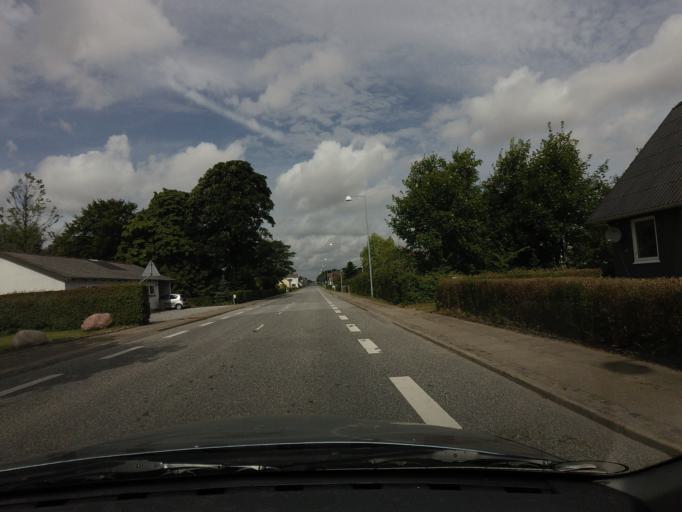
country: DK
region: North Denmark
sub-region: Hjorring Kommune
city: Sindal
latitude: 57.3356
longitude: 10.3112
